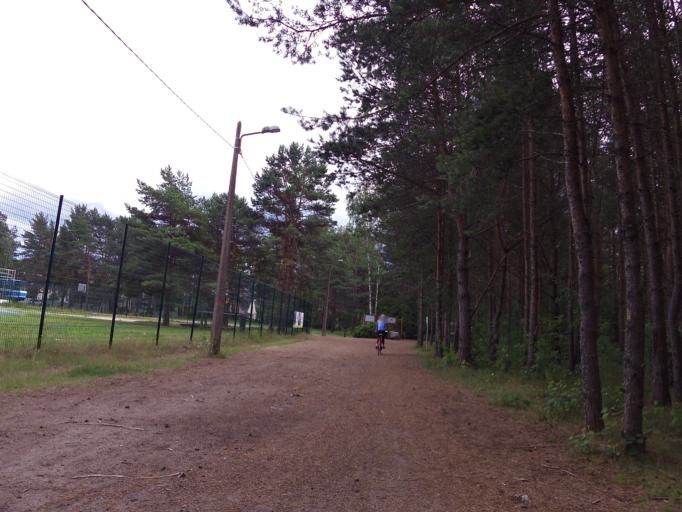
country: EE
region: Harju
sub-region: Saue vald
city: Laagri
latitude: 59.3853
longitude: 24.6578
